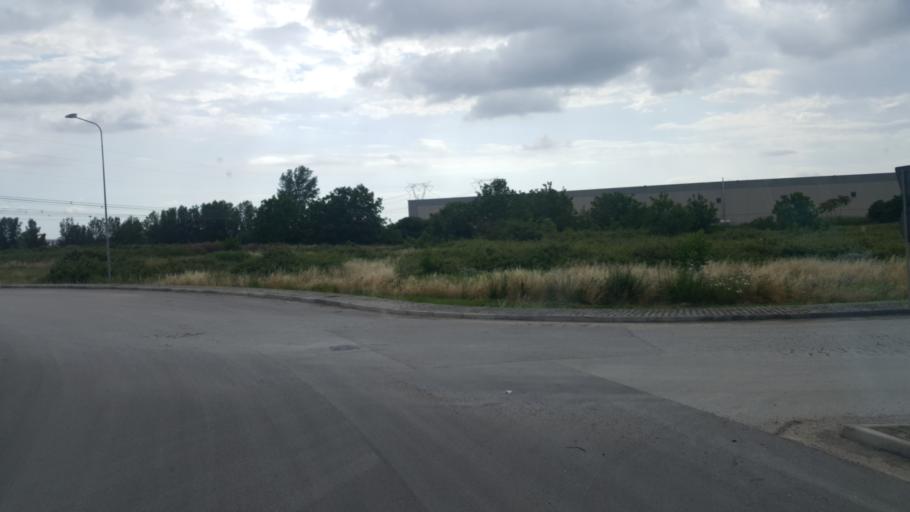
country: IT
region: Campania
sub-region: Provincia di Caserta
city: San Marco Evangelista
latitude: 41.0084
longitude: 14.3550
